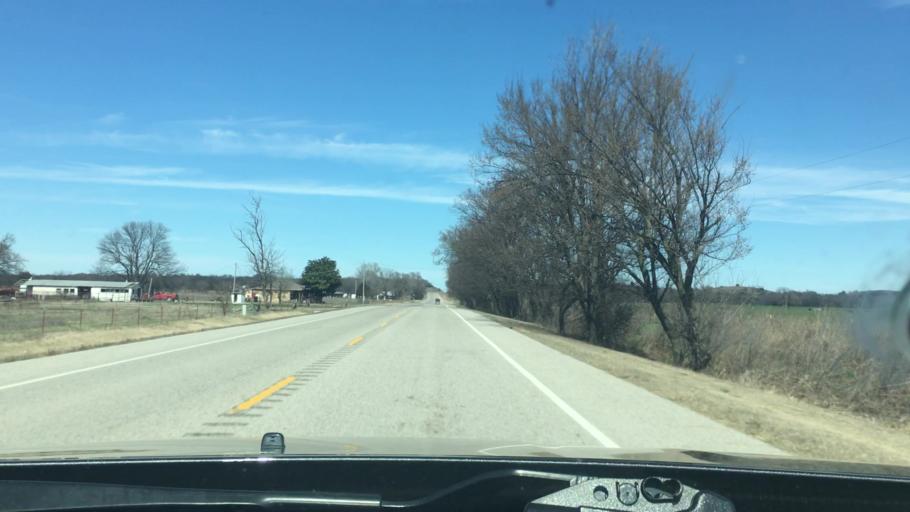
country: US
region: Oklahoma
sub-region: Murray County
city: Sulphur
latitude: 34.3933
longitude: -96.9511
